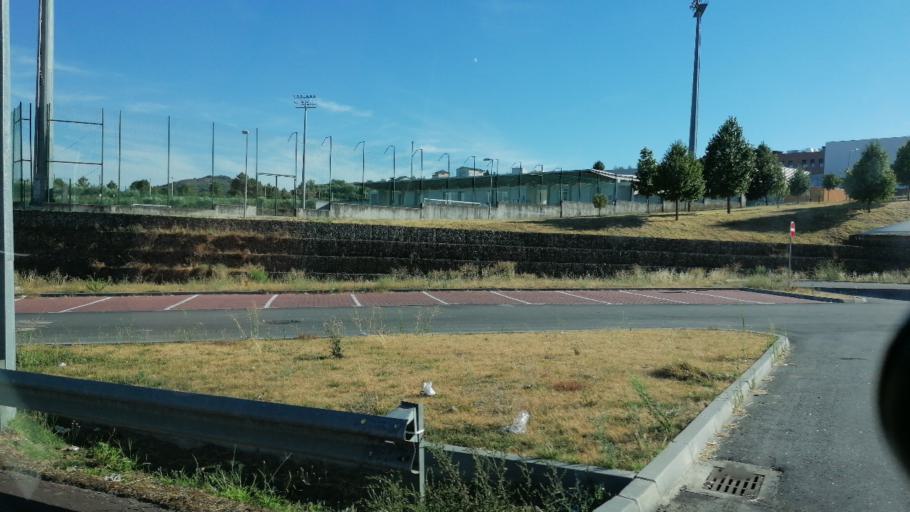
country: PT
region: Vila Real
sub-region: Murca
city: Murca
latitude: 41.4044
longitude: -7.4486
